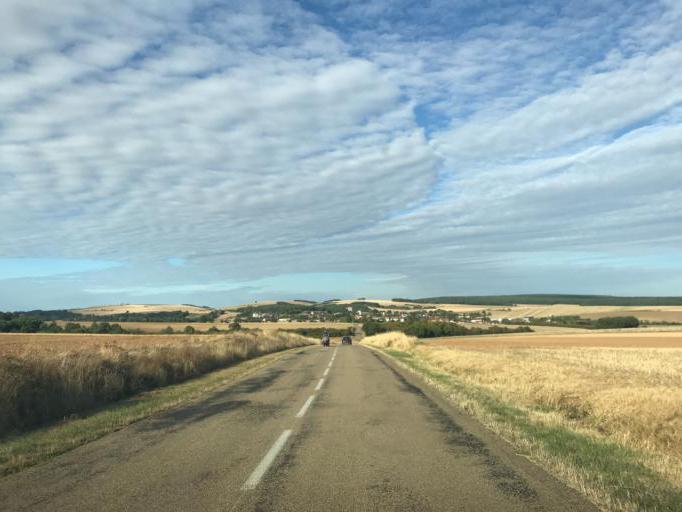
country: FR
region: Bourgogne
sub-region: Departement de l'Yonne
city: Fontenailles
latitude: 47.6038
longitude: 3.4844
